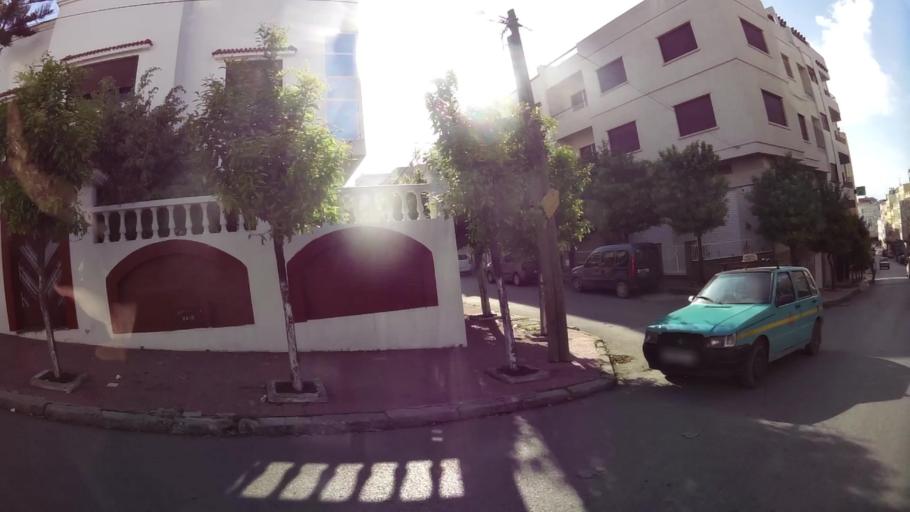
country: MA
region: Tanger-Tetouan
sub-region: Tanger-Assilah
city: Tangier
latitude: 35.7668
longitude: -5.7951
